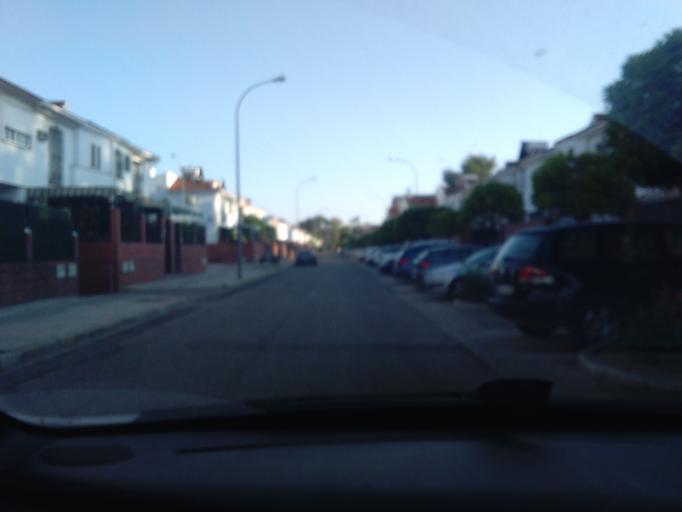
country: ES
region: Andalusia
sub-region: Provincia de Sevilla
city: Sevilla
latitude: 37.4110
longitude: -5.9367
